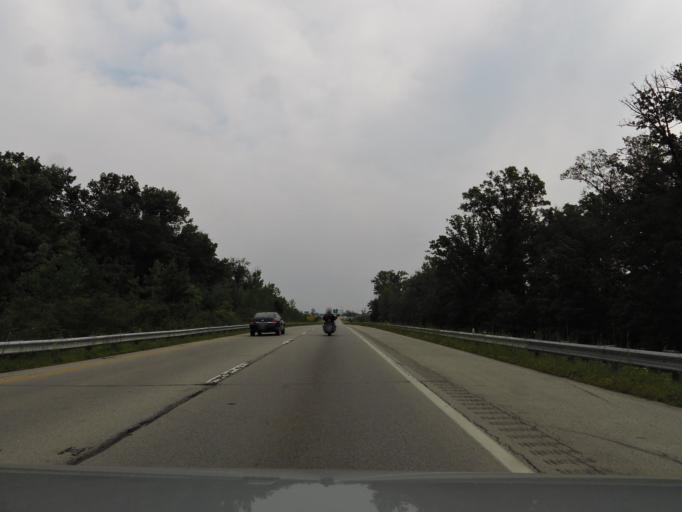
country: US
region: Ohio
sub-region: Montgomery County
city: West Carrollton City
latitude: 39.6177
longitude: -84.2298
